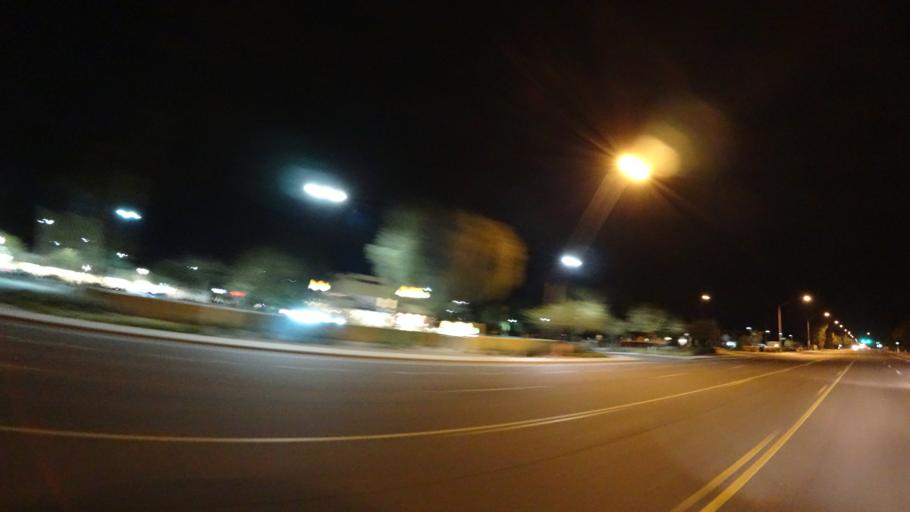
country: US
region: Arizona
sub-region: Maricopa County
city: Gilbert
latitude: 33.3937
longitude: -111.7518
